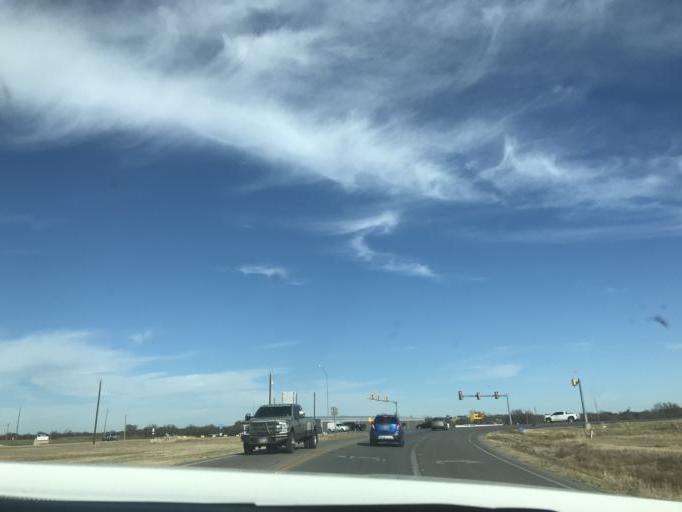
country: US
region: Texas
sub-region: Erath County
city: Stephenville
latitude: 32.2431
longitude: -98.1960
